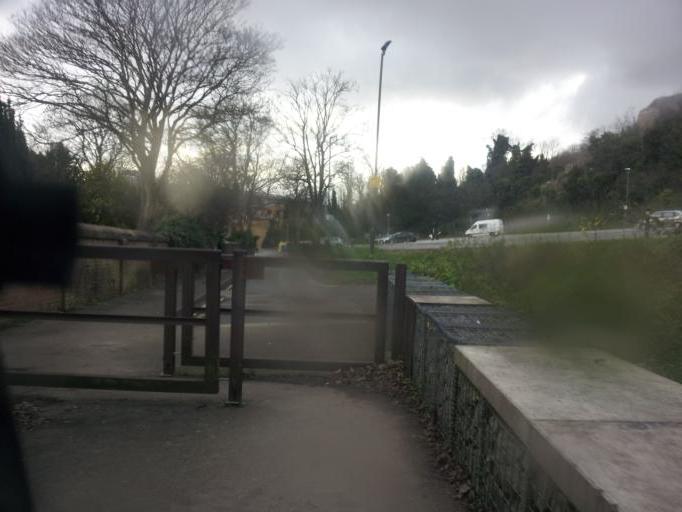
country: GB
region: England
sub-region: Kent
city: Chatham
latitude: 51.3845
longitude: 0.5282
